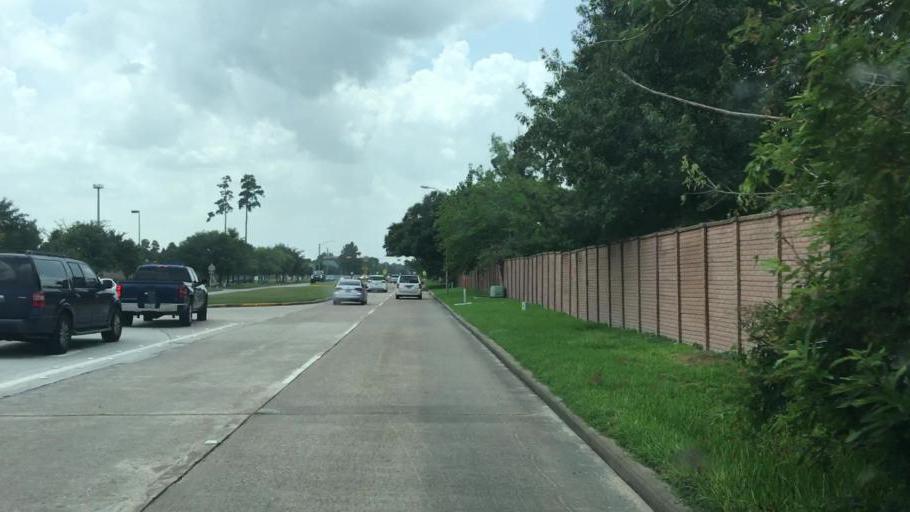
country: US
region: Texas
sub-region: Harris County
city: Atascocita
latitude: 29.9946
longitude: -95.1618
